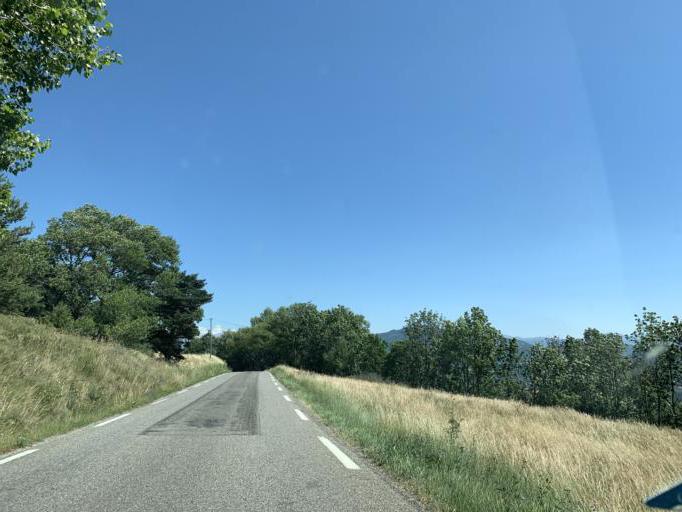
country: FR
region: Provence-Alpes-Cote d'Azur
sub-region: Departement des Hautes-Alpes
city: La Batie-Neuve
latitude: 44.5980
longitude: 6.1472
